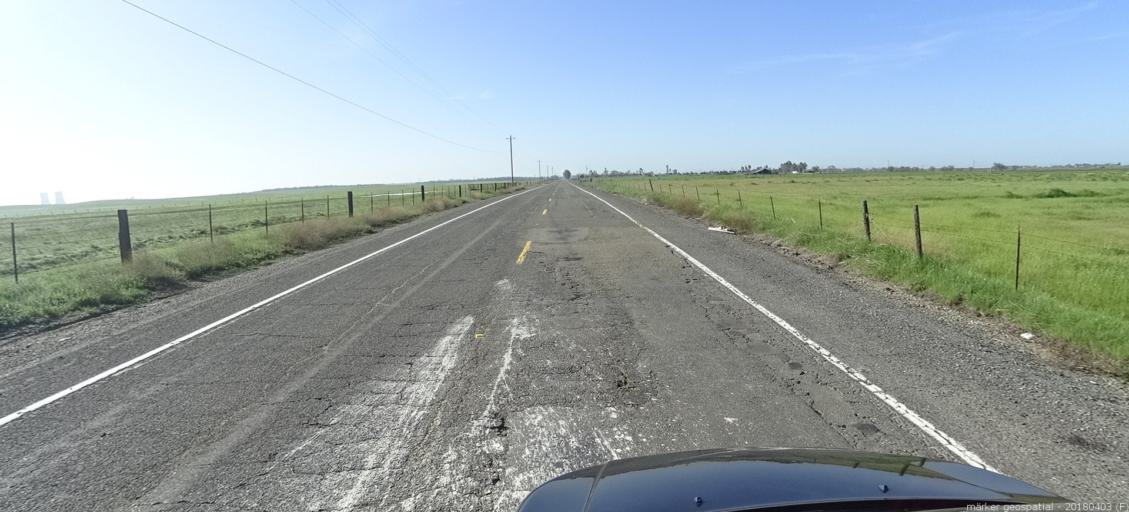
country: US
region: California
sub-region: Sacramento County
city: Clay
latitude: 38.3813
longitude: -121.1685
